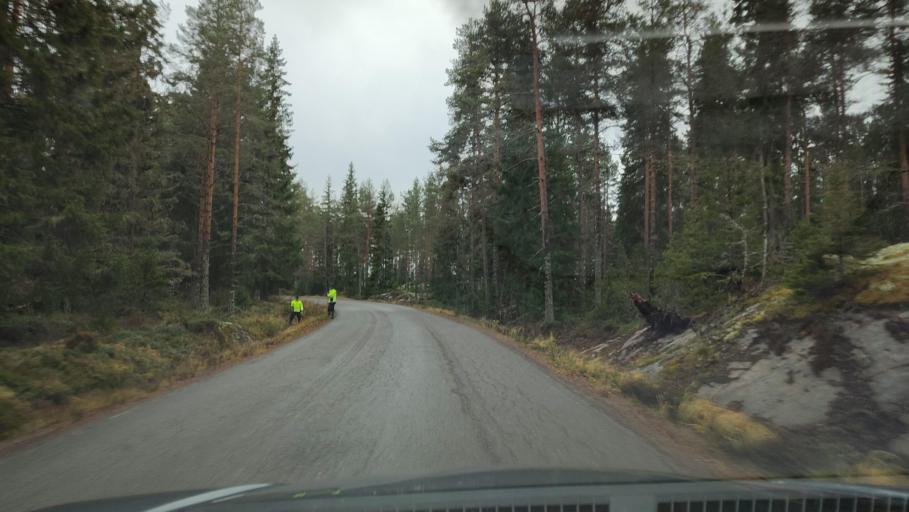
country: FI
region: Southern Ostrobothnia
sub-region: Suupohja
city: Karijoki
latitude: 62.1326
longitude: 21.5759
